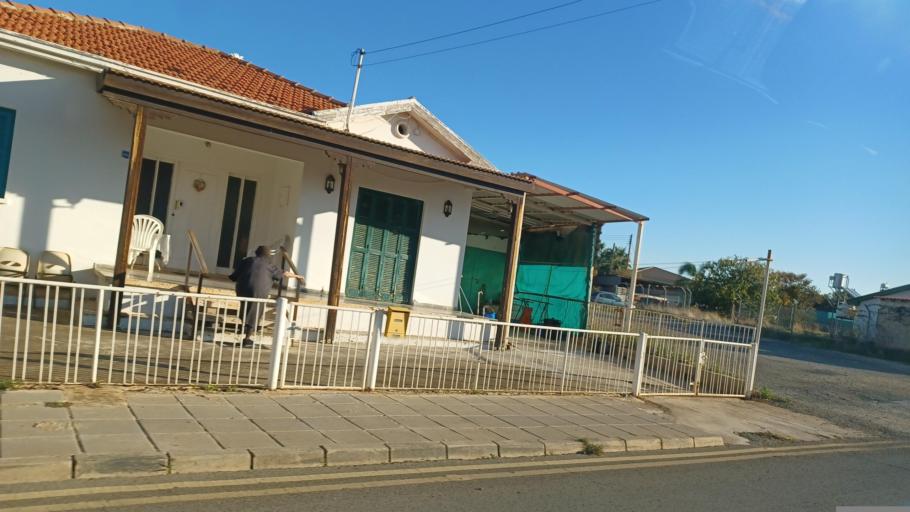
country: CY
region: Lefkosia
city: Astromeritis
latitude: 35.1397
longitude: 33.0465
